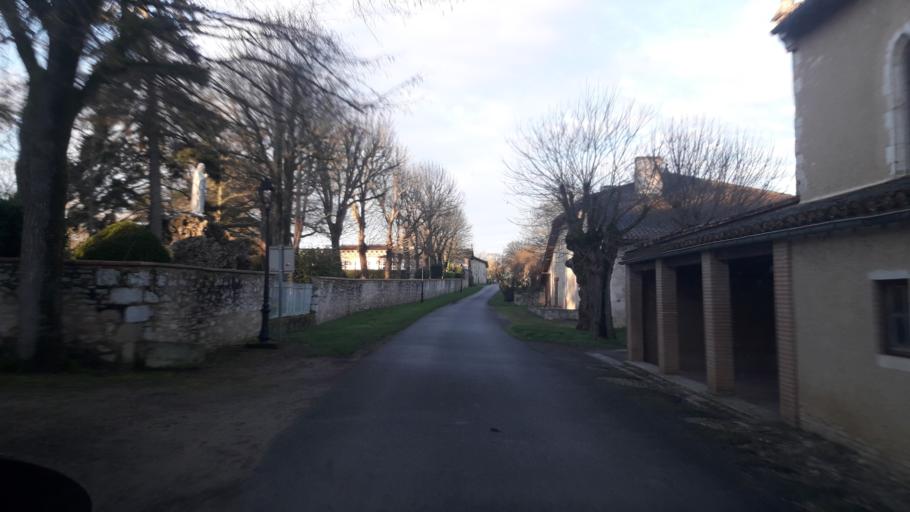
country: FR
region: Midi-Pyrenees
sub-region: Departement du Gers
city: Gimont
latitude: 43.7099
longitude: 0.9500
